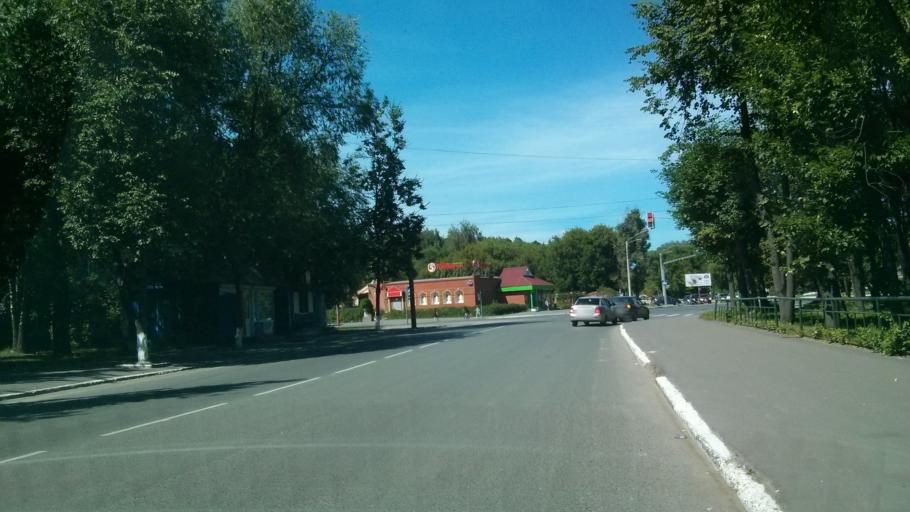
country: RU
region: Vladimir
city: Murom
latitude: 55.5738
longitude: 42.0281
